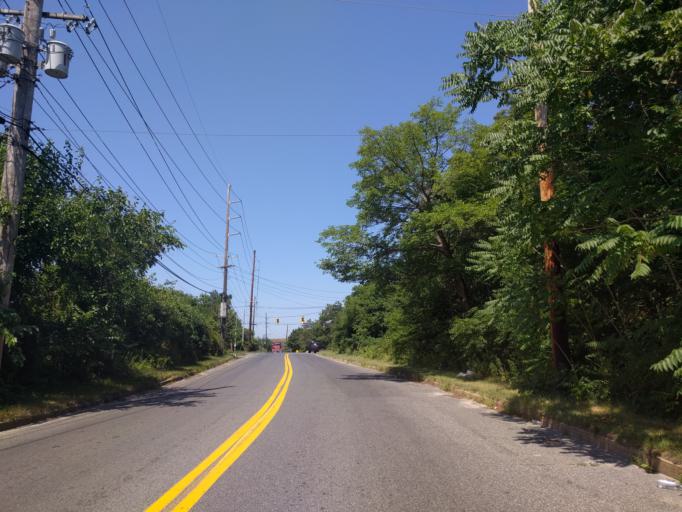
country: US
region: New York
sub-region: Suffolk County
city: Kings Park
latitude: 40.8750
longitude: -73.2778
